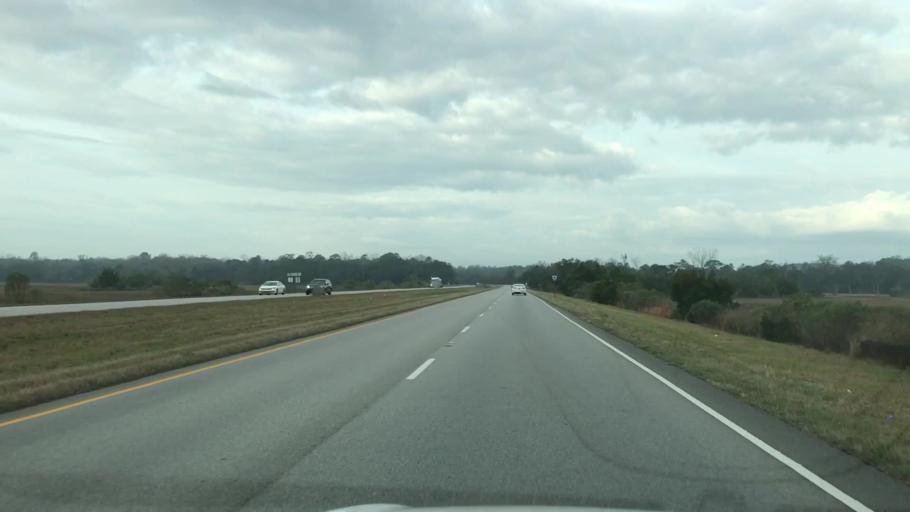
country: US
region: South Carolina
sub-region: Hampton County
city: Yemassee
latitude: 32.5999
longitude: -80.7732
